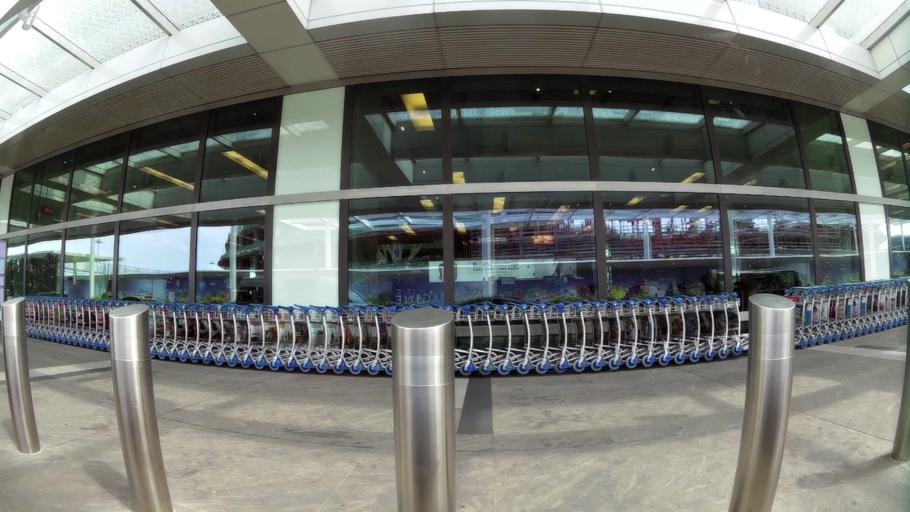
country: SG
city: Singapore
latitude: 1.3612
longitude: 103.9900
